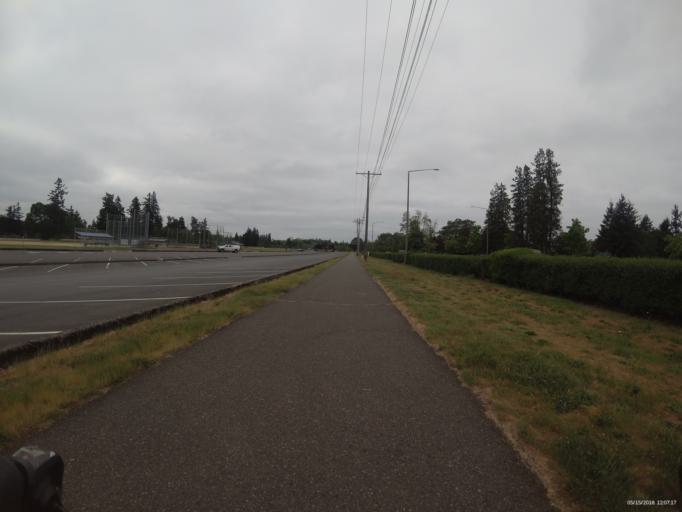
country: US
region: Washington
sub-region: Pierce County
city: Lakewood
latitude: 47.1787
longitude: -122.5555
